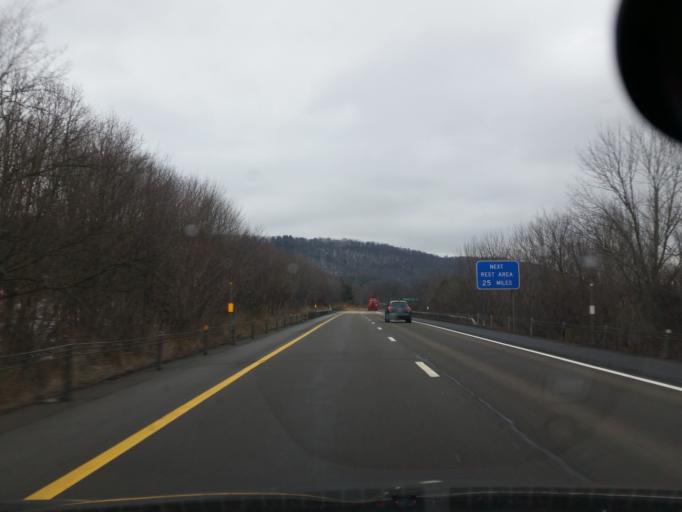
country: US
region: Pennsylvania
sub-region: Susquehanna County
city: Hallstead
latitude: 42.0080
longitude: -75.7588
